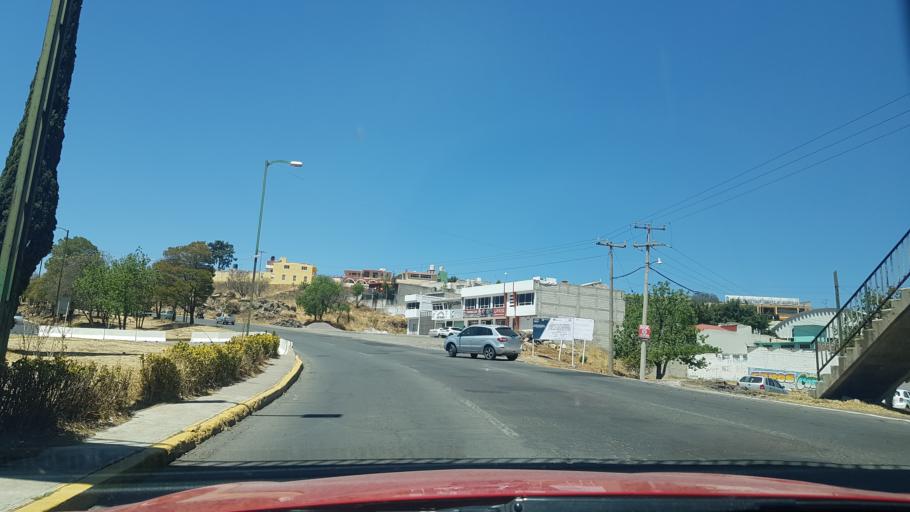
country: MX
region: Mexico
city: Atlacomulco
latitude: 19.8069
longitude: -99.8749
